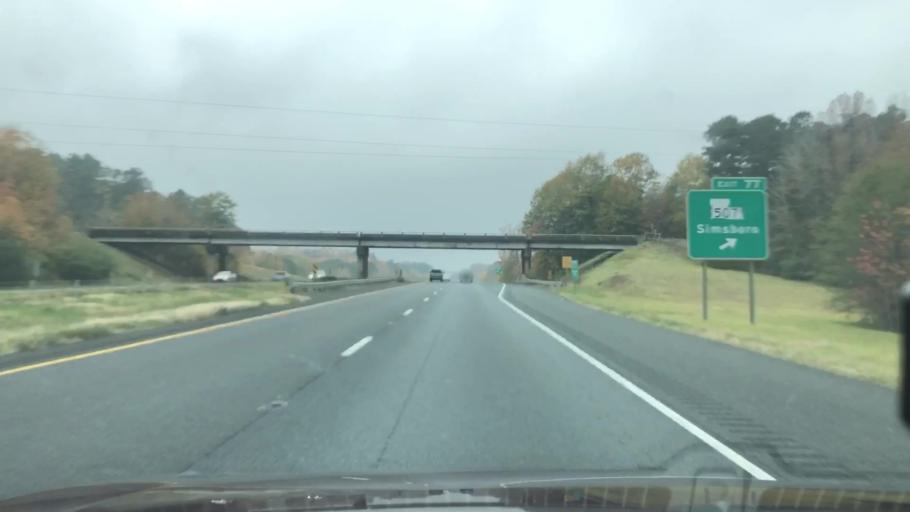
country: US
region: Louisiana
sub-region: Lincoln Parish
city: Grambling
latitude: 32.5486
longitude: -92.7863
